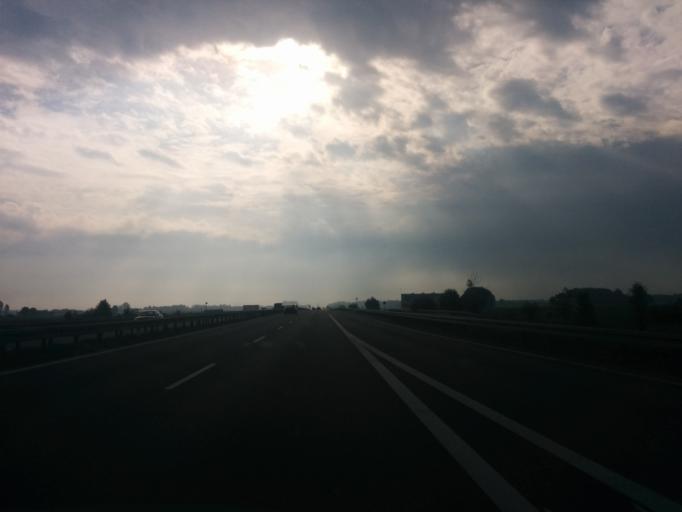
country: PL
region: Masovian Voivodeship
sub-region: Powiat radomski
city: Jedlinsk
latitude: 51.5413
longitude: 21.0621
